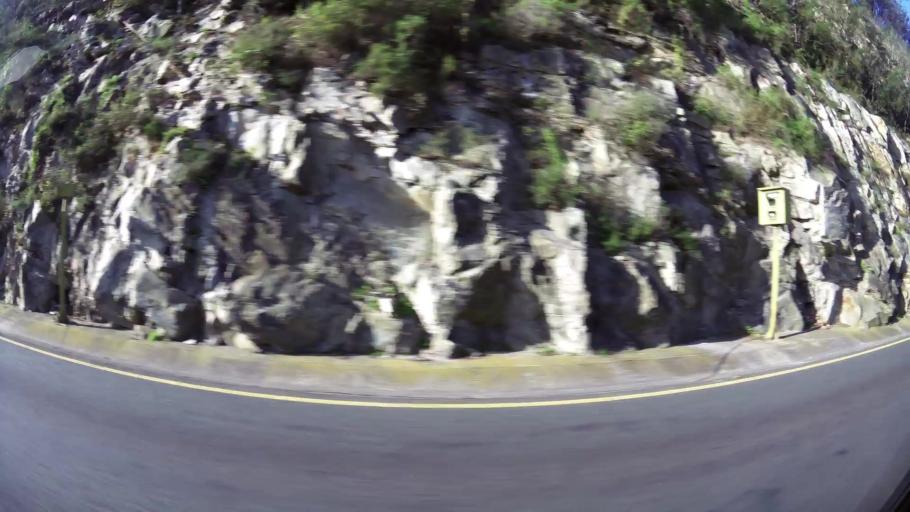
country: ZA
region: Western Cape
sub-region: Eden District Municipality
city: George
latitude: -33.9894
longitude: 22.5468
